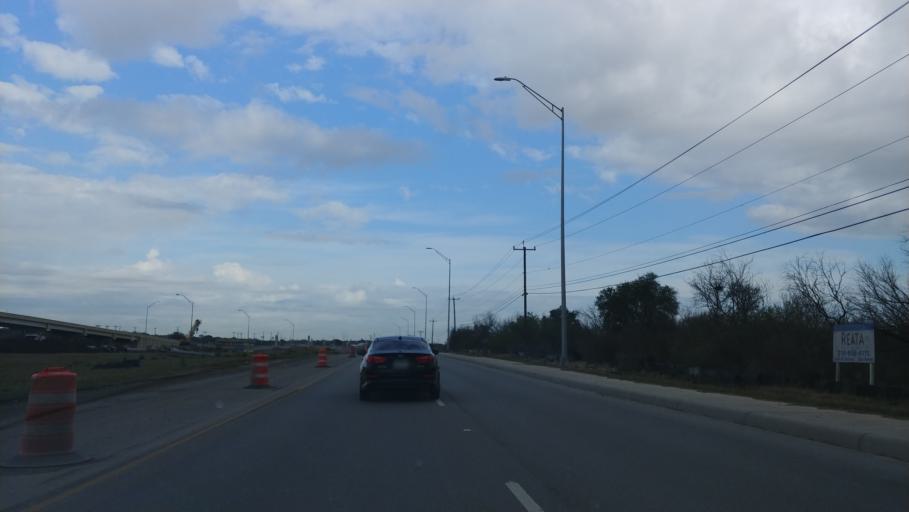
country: US
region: Texas
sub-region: Bexar County
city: Lackland Air Force Base
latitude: 29.3864
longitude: -98.7009
